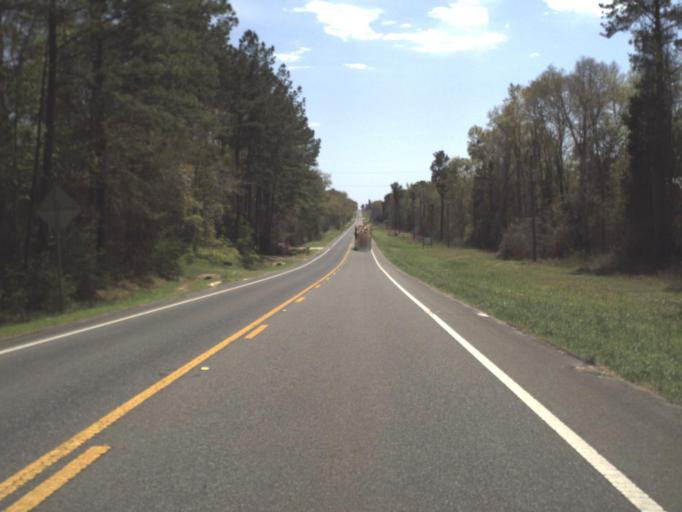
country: US
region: Florida
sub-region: Walton County
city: DeFuniak Springs
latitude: 30.7812
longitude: -85.9587
